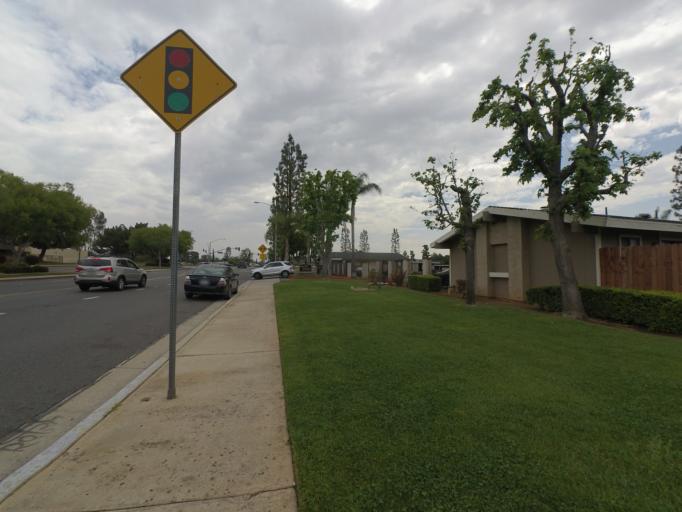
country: US
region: California
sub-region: Riverside County
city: Moreno Valley
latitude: 33.9317
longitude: -117.2454
